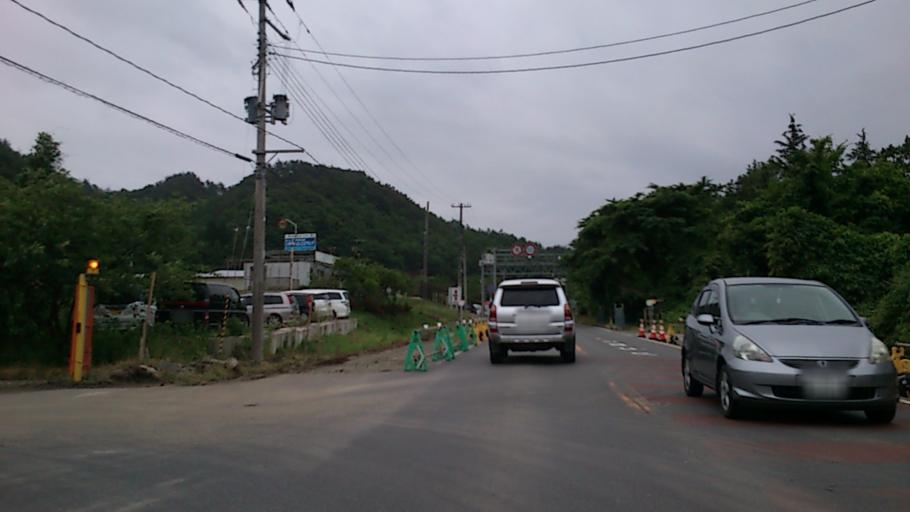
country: JP
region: Fukushima
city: Fukushima-shi
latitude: 37.7081
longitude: 140.5062
